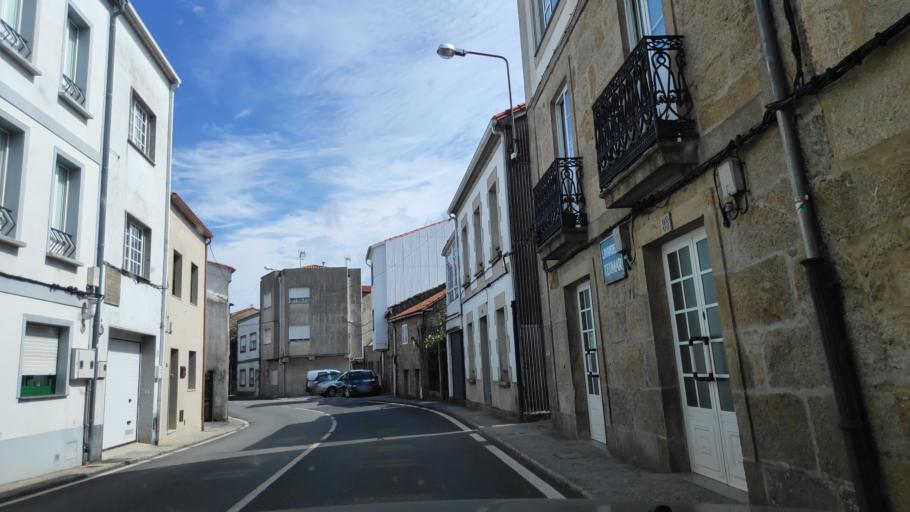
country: ES
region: Galicia
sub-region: Provincia da Coruna
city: Padron
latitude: 42.7377
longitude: -8.6632
